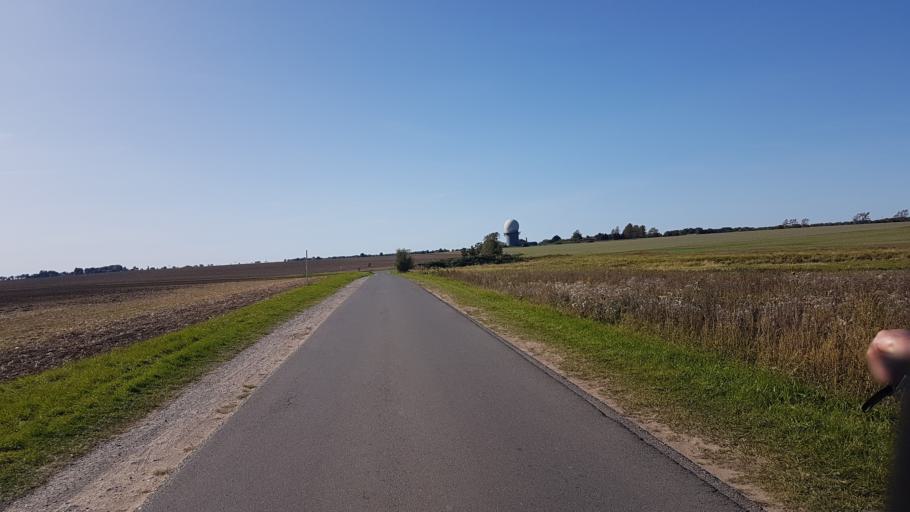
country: DE
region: Mecklenburg-Vorpommern
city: Altenkirchen
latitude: 54.6726
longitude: 13.4008
